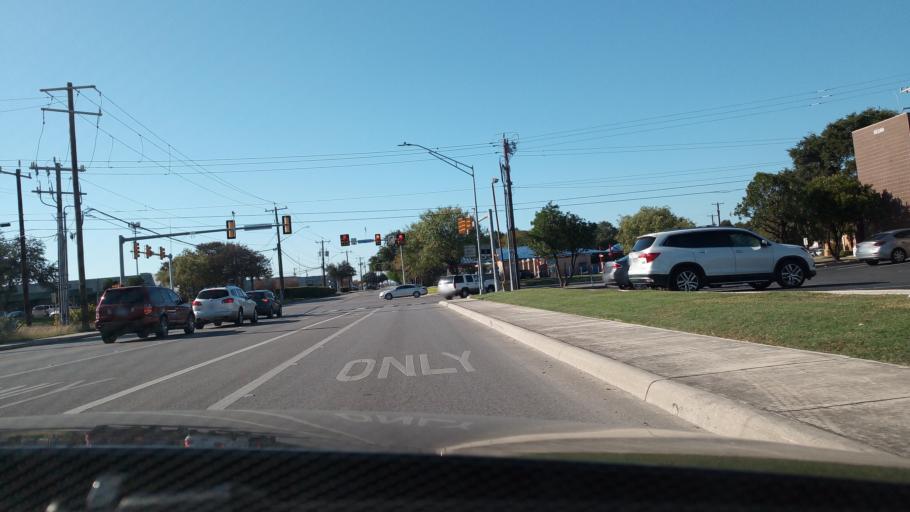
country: US
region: Texas
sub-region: Bexar County
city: Alamo Heights
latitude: 29.5325
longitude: -98.4478
